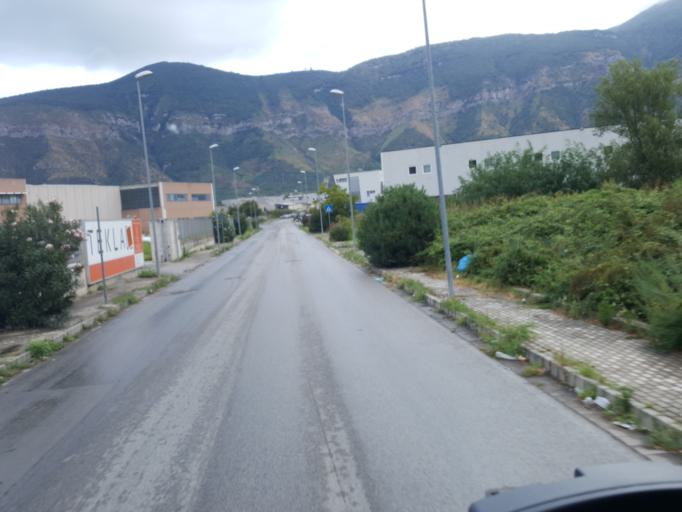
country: IT
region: Campania
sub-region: Provincia di Salerno
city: Sarno
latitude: 40.8153
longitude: 14.5997
